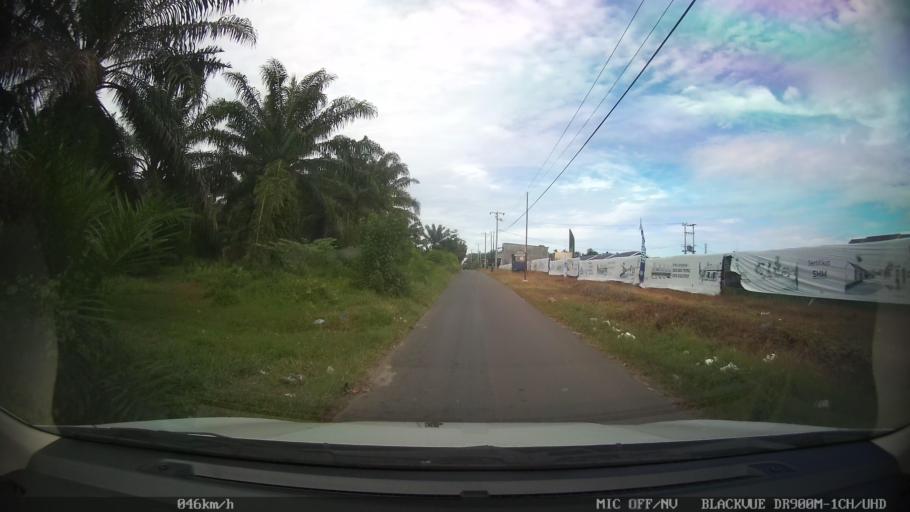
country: ID
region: North Sumatra
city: Sunggal
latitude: 3.5726
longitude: 98.5697
